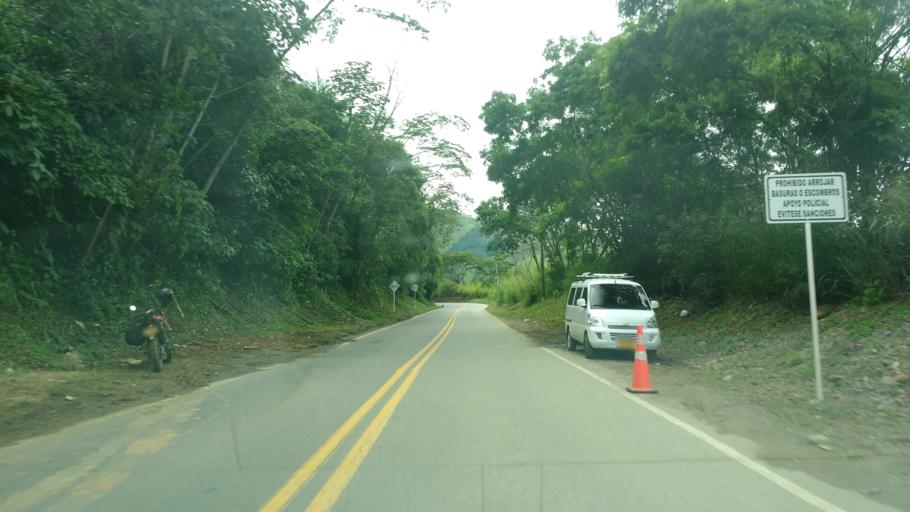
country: CO
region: Antioquia
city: Amaga
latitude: 6.0620
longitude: -75.7345
